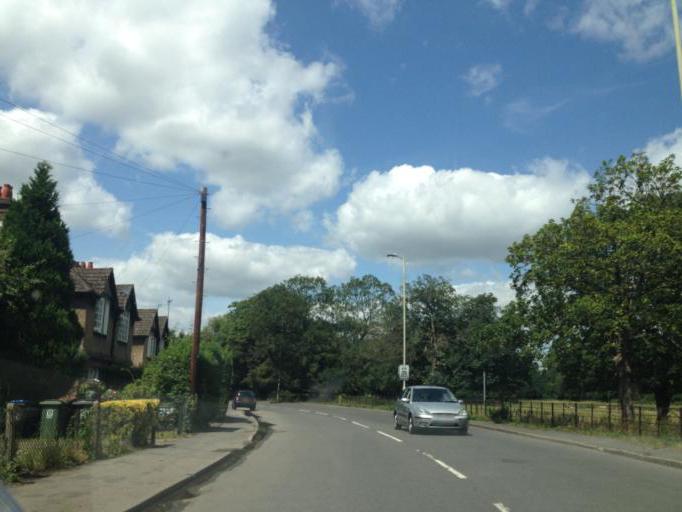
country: GB
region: England
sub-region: Hertfordshire
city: Hemel Hempstead
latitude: 51.7412
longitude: -0.4772
